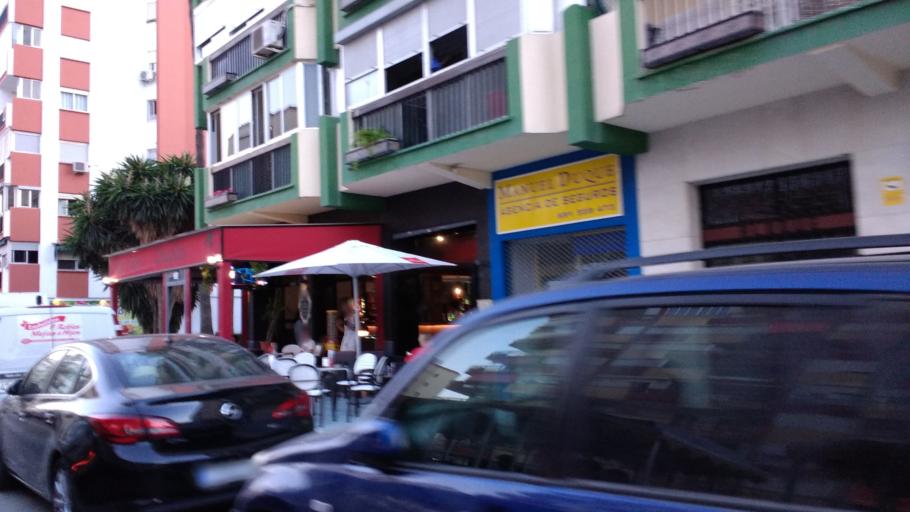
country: ES
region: Andalusia
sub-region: Provincia de Malaga
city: Velez-Malaga
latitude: 36.7379
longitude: -4.0989
